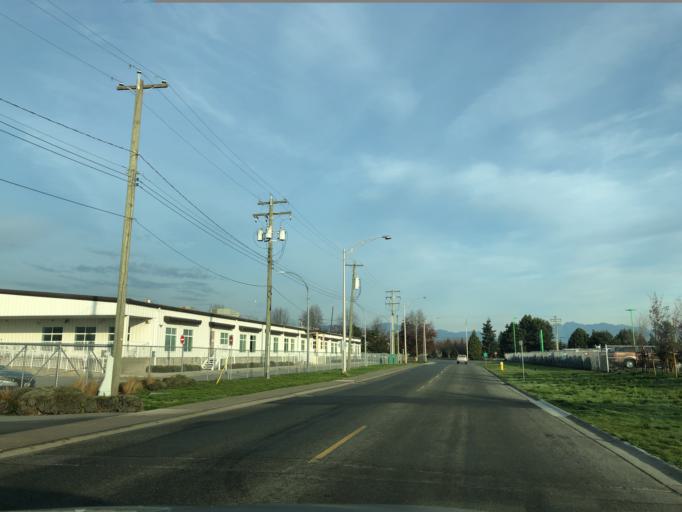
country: CA
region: British Columbia
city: Richmond
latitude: 49.1906
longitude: -123.1541
